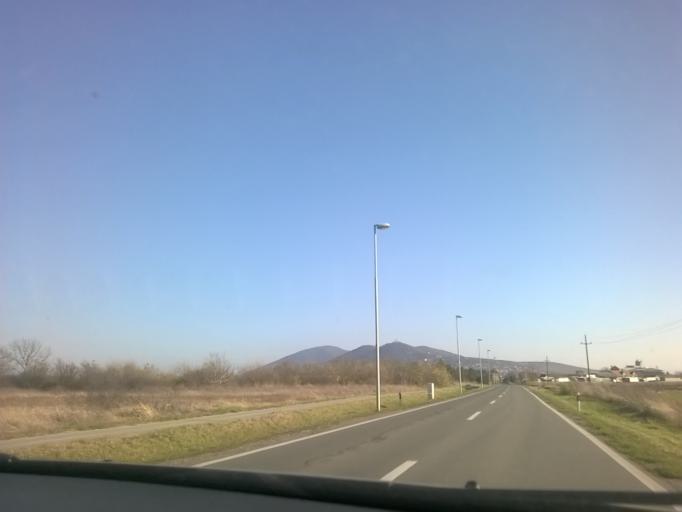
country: RS
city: Pavlis
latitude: 45.1125
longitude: 21.2698
